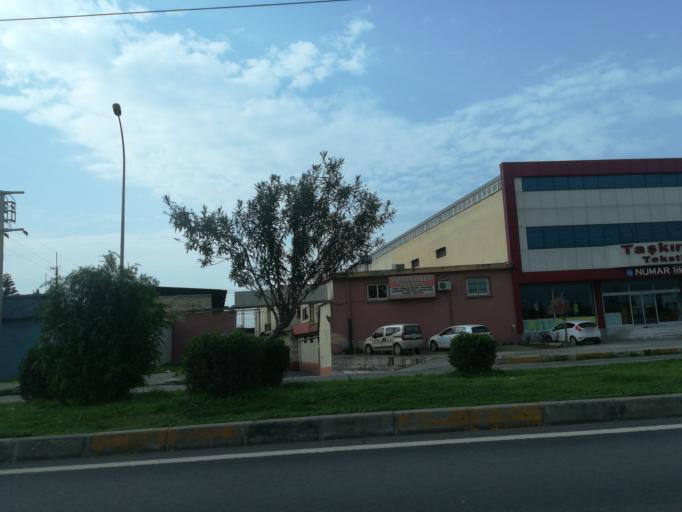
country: TR
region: Adana
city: Yuregir
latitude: 36.9860
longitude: 35.3619
